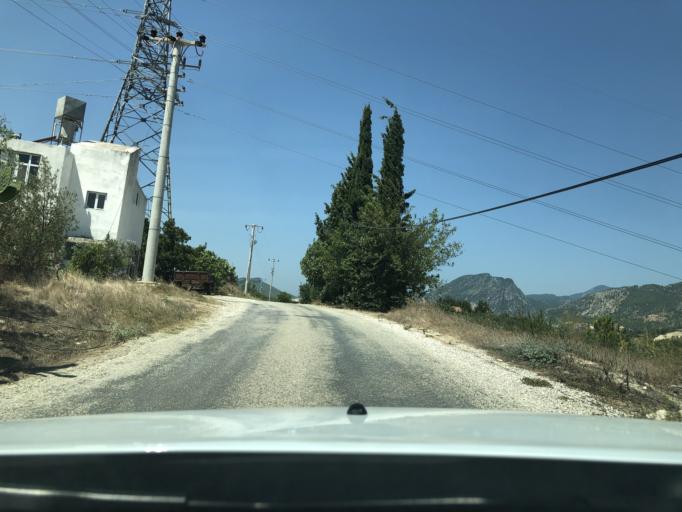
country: TR
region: Antalya
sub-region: Manavgat
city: Kizilagac
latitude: 36.8564
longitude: 31.5581
